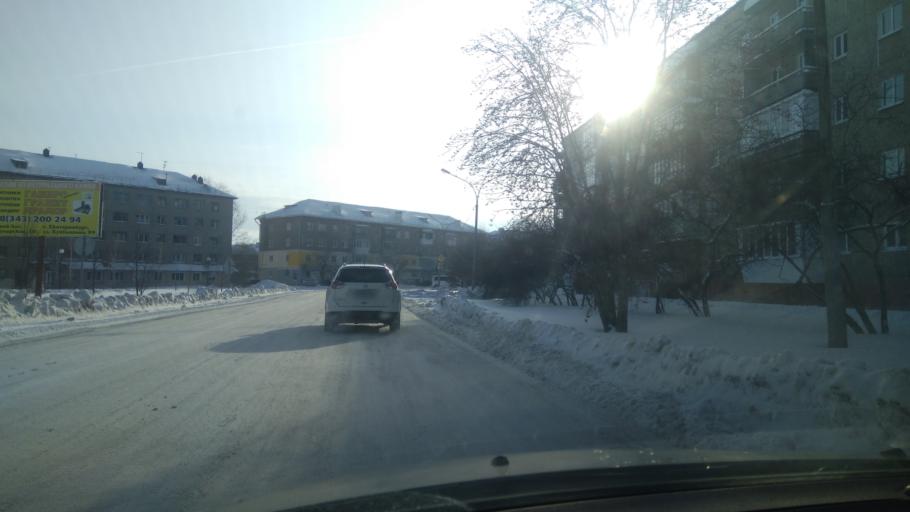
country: RU
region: Sverdlovsk
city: Sukhoy Log
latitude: 56.9092
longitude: 62.0336
